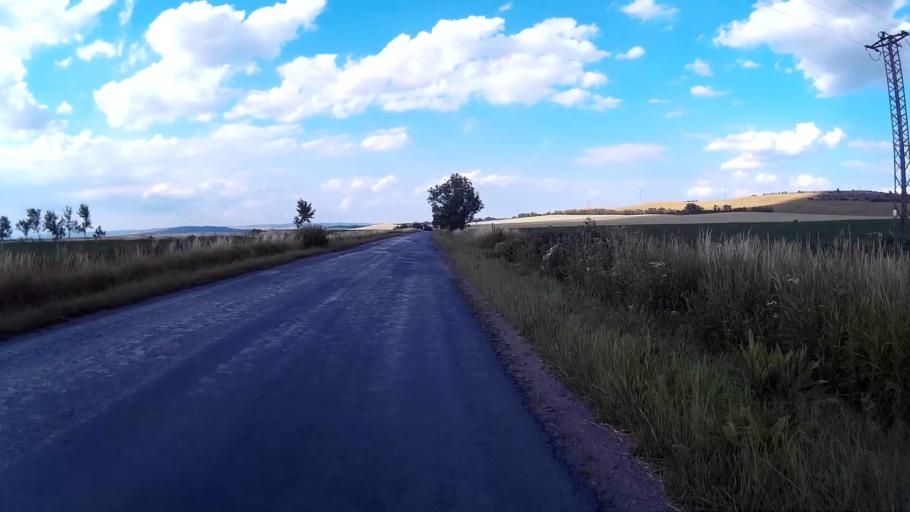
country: CZ
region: South Moravian
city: Tesany
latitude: 49.0470
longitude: 16.7736
